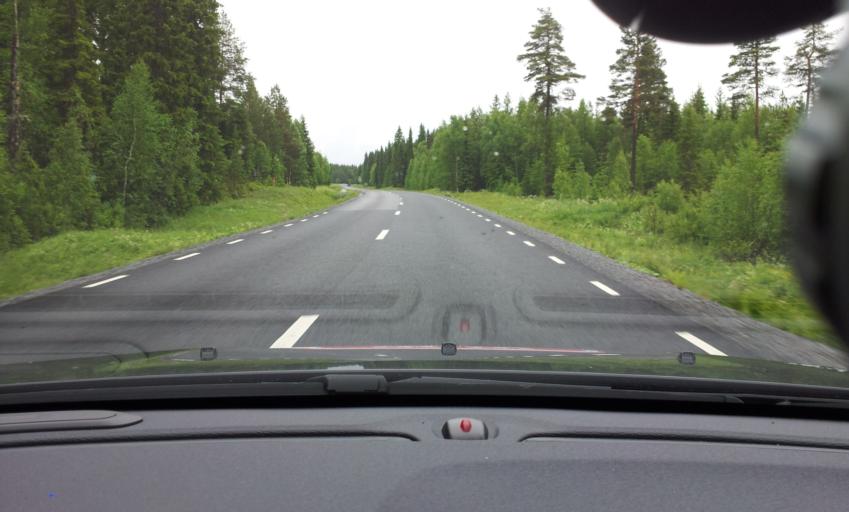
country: SE
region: Jaemtland
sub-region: Stroemsunds Kommun
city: Stroemsund
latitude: 63.6374
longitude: 15.1922
